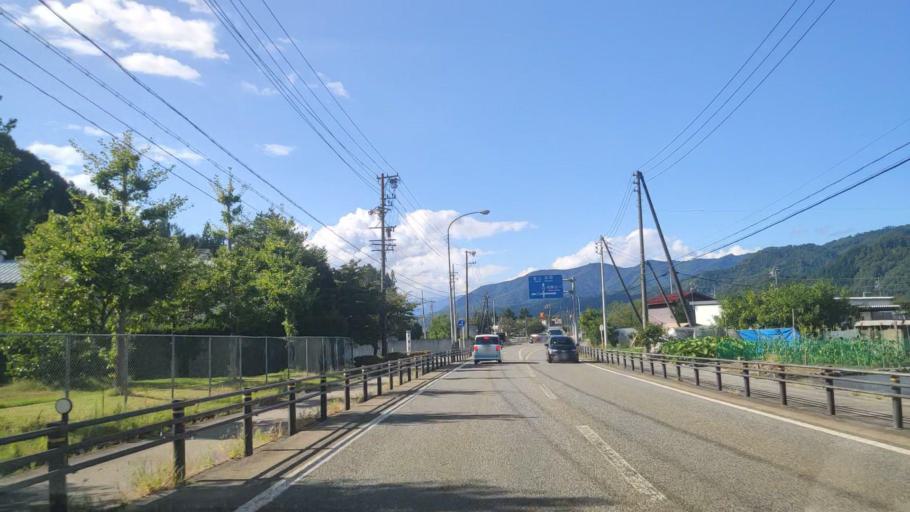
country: JP
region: Gifu
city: Takayama
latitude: 36.2387
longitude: 137.1748
